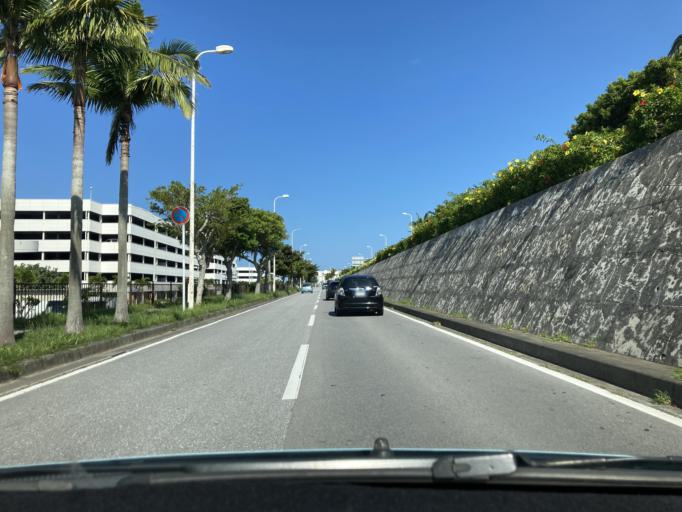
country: JP
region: Okinawa
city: Naha-shi
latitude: 26.2073
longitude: 127.6523
